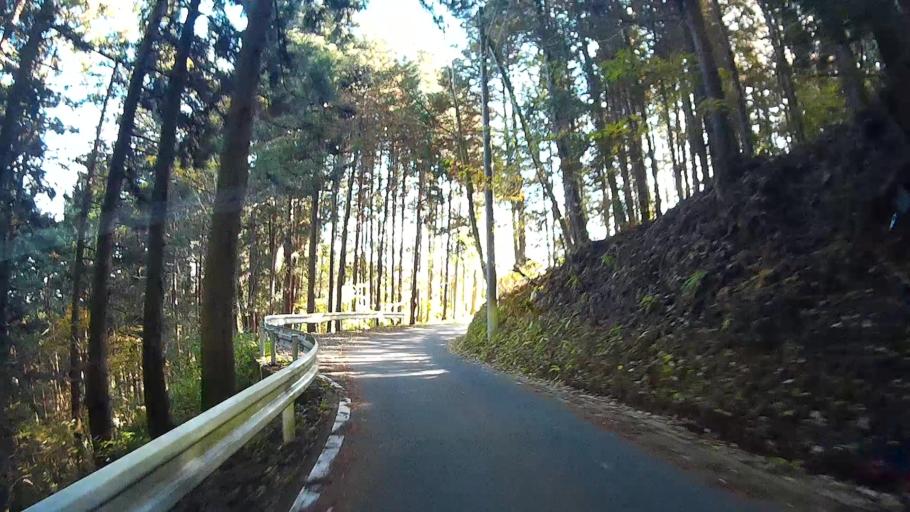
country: JP
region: Yamanashi
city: Uenohara
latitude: 35.5896
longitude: 139.1295
